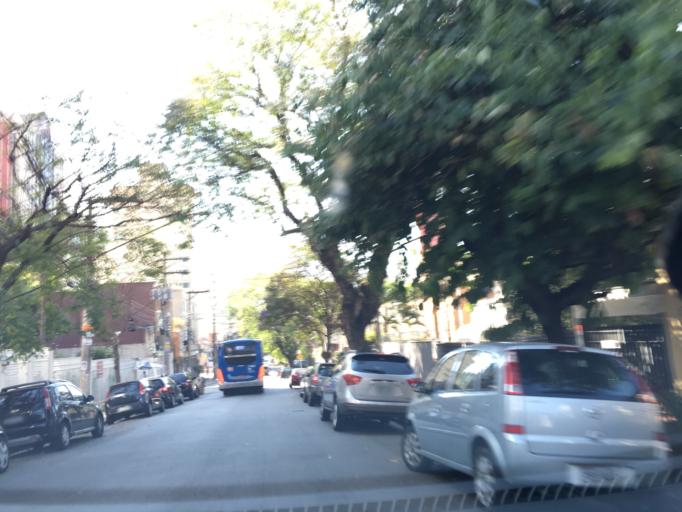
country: BR
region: Sao Paulo
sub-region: Sao Paulo
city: Sao Paulo
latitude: -23.5345
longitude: -46.6632
